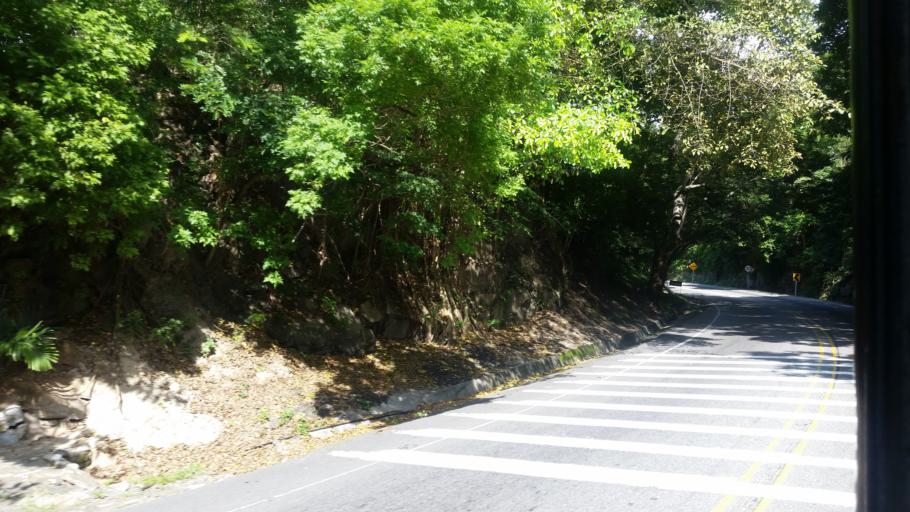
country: CO
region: Magdalena
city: Santa Marta
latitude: 11.2660
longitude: -74.0760
